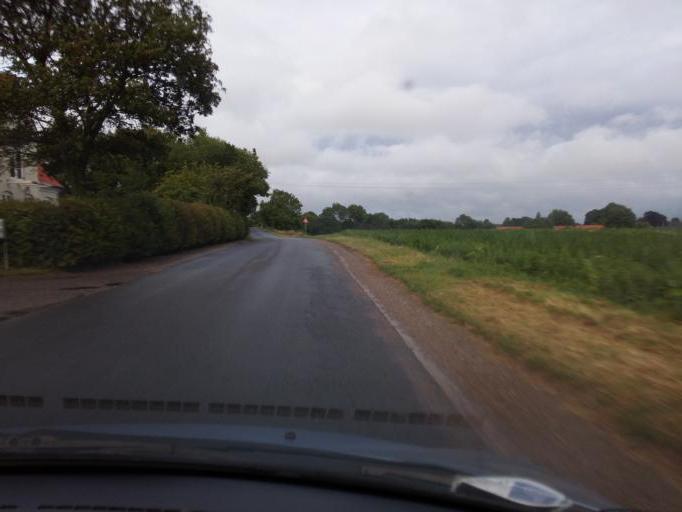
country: DK
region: South Denmark
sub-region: Kerteminde Kommune
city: Kerteminde
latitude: 55.5036
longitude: 10.6418
